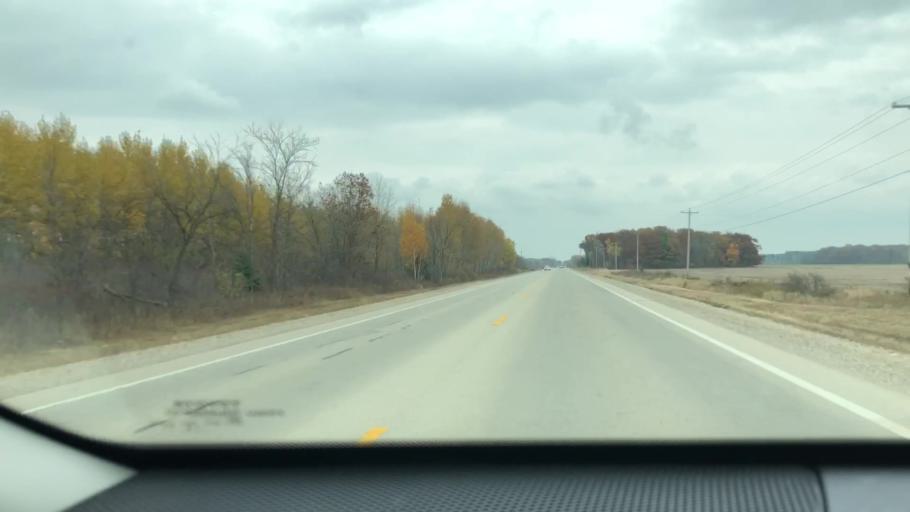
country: US
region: Wisconsin
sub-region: Brown County
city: Oneida
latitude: 44.5021
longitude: -88.2196
